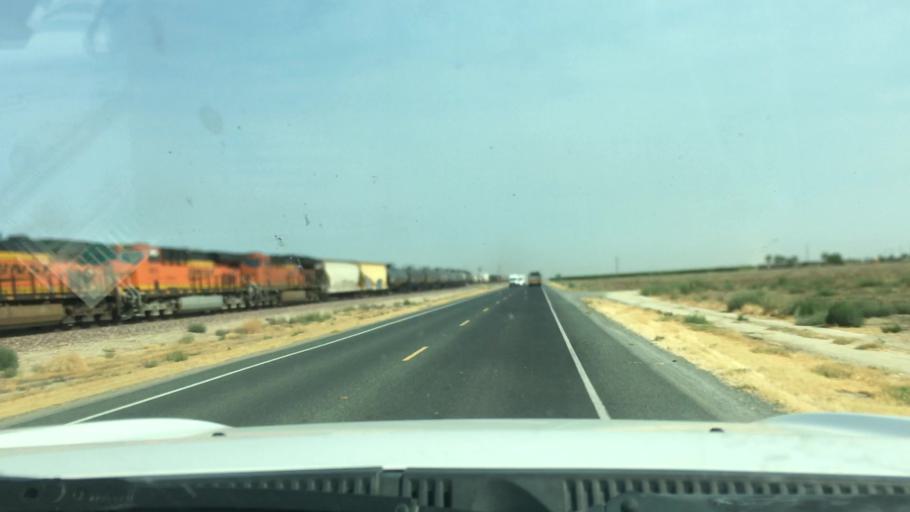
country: US
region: California
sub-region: Kern County
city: Delano
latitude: 35.7713
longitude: -119.3486
